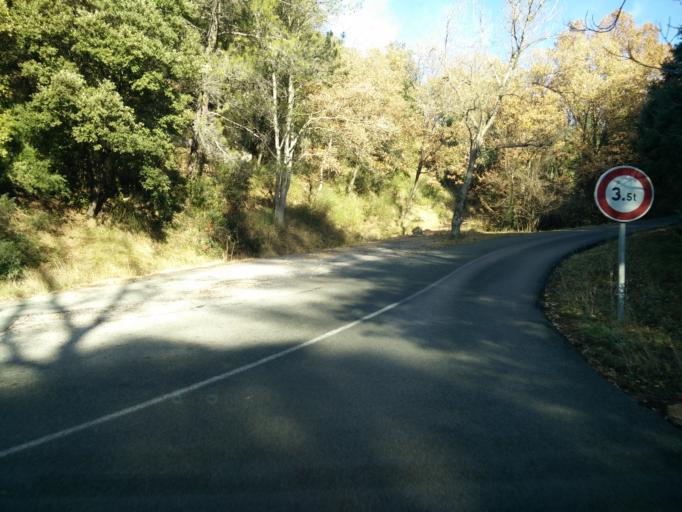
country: FR
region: Provence-Alpes-Cote d'Azur
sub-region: Departement du Var
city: Taradeau
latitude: 43.4550
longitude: 6.4288
